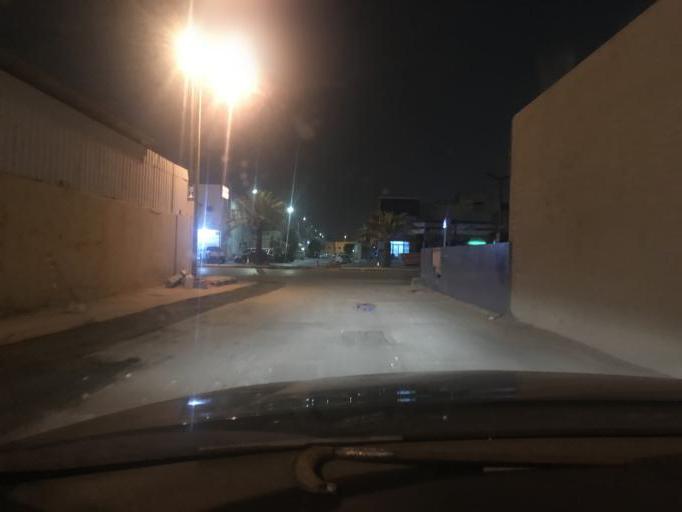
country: SA
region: Ar Riyad
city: Riyadh
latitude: 24.7492
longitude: 46.7772
